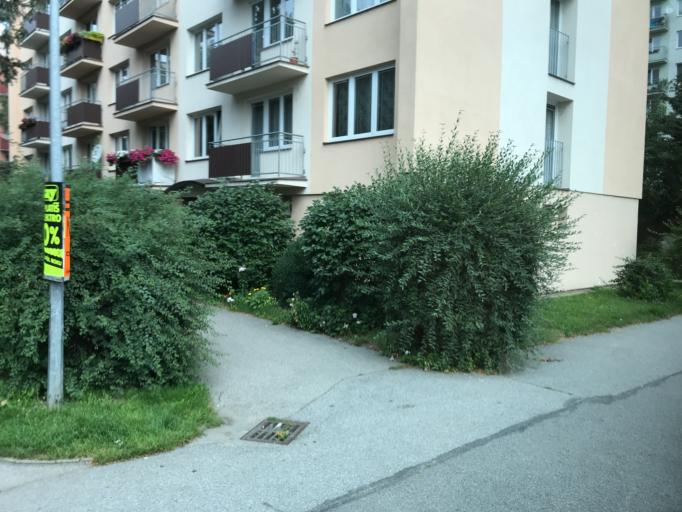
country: CZ
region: Jihocesky
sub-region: Okres Ceske Budejovice
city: Ceske Budejovice
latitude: 48.9676
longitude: 14.4747
